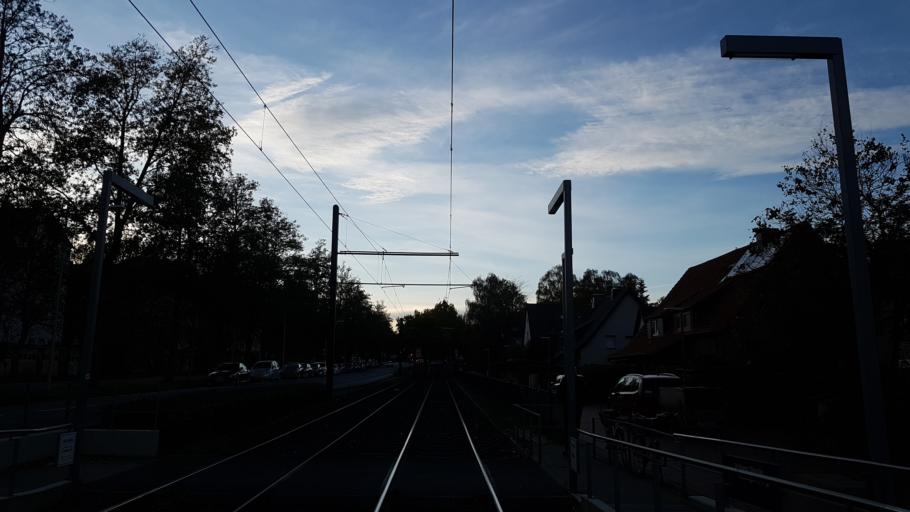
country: DE
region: Lower Saxony
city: Hemmingen
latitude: 52.3415
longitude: 9.7015
